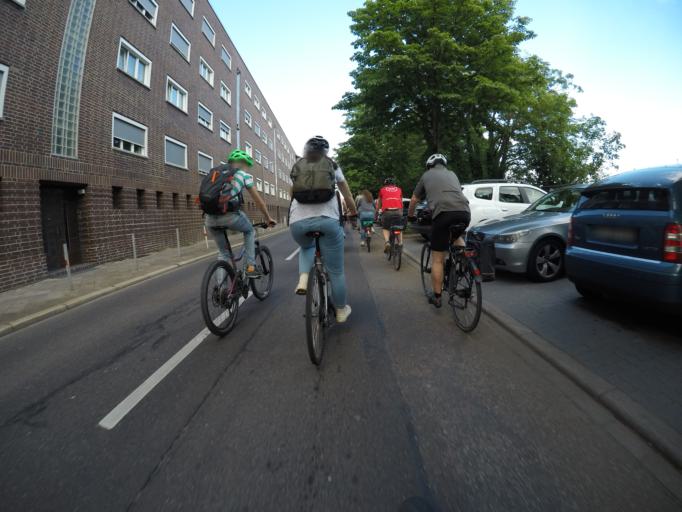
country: DE
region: Baden-Wuerttemberg
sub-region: Karlsruhe Region
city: Karlsruhe
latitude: 48.9978
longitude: 8.4137
